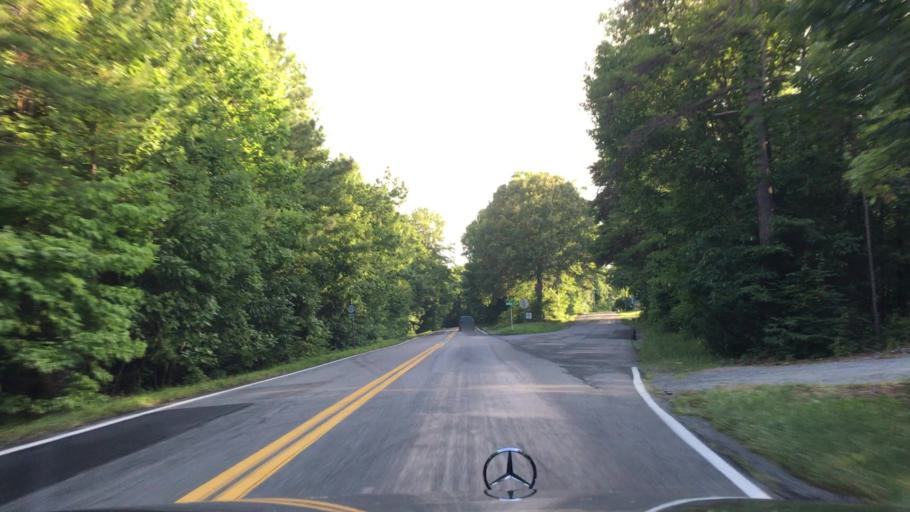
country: US
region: Virginia
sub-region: Campbell County
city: Timberlake
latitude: 37.2492
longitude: -79.2805
